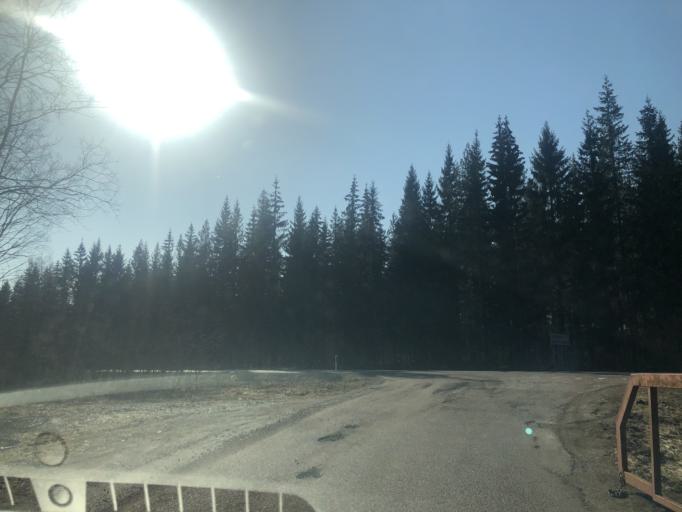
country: SE
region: Vaermland
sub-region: Filipstads Kommun
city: Filipstad
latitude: 59.7835
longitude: 14.2593
